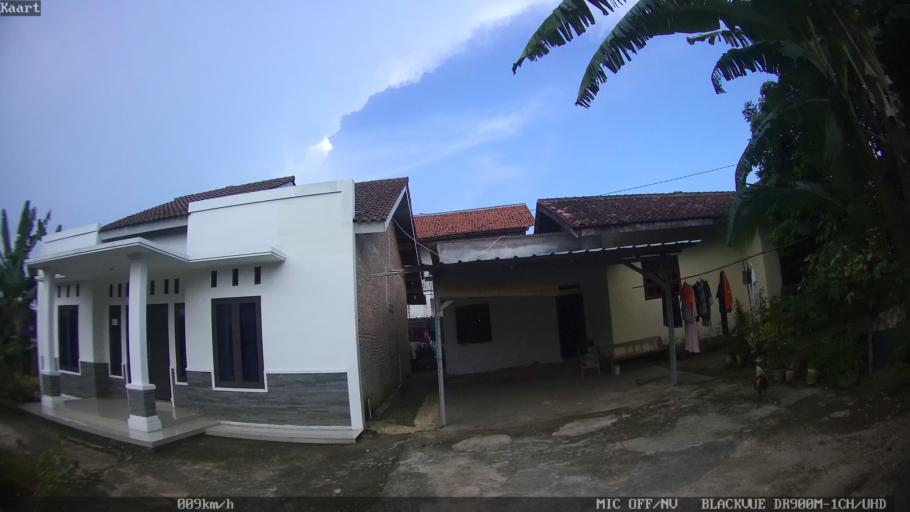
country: ID
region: Lampung
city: Kedaton
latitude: -5.3941
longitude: 105.2080
